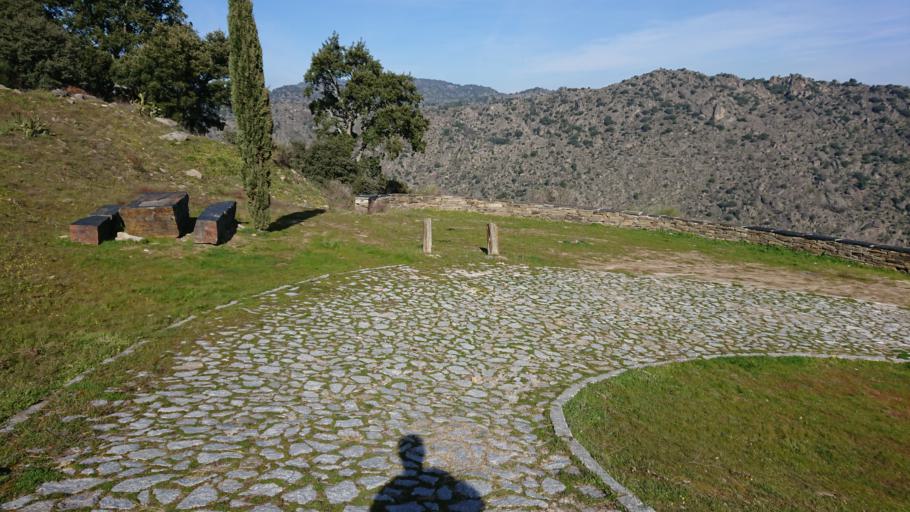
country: PT
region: Viseu
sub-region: Sao Joao da Pesqueira
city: Sao Joao da Pesqueira
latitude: 41.1512
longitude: -7.3658
